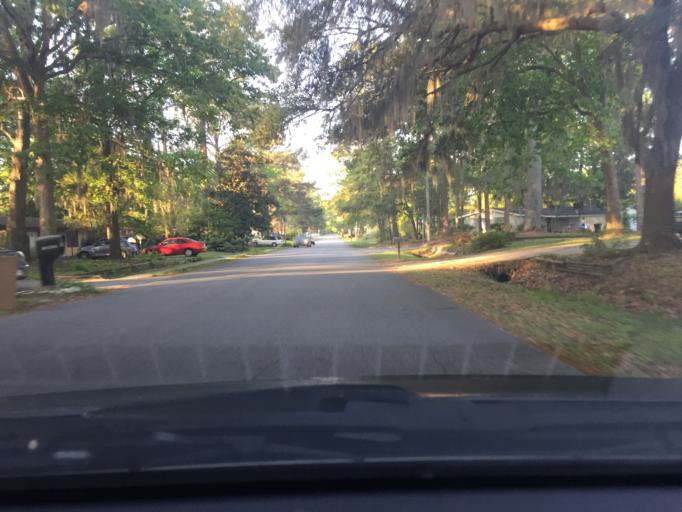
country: US
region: Georgia
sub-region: Chatham County
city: Montgomery
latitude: 31.9755
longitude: -81.1463
